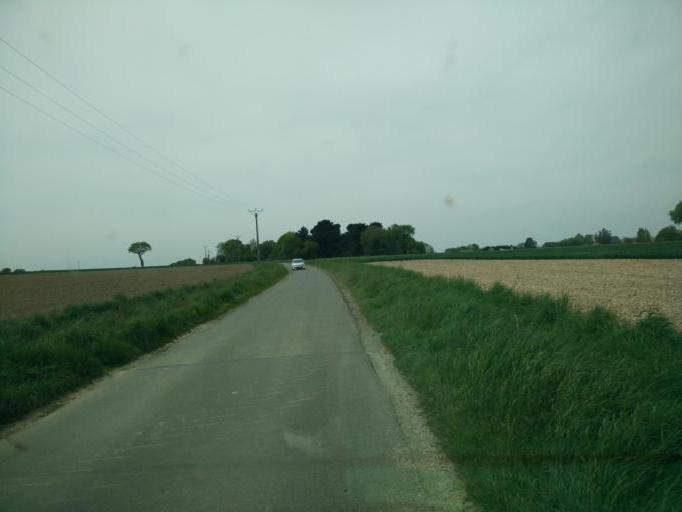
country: FR
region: Brittany
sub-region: Departement des Cotes-d'Armor
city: Crehen
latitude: 48.5754
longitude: -2.1909
